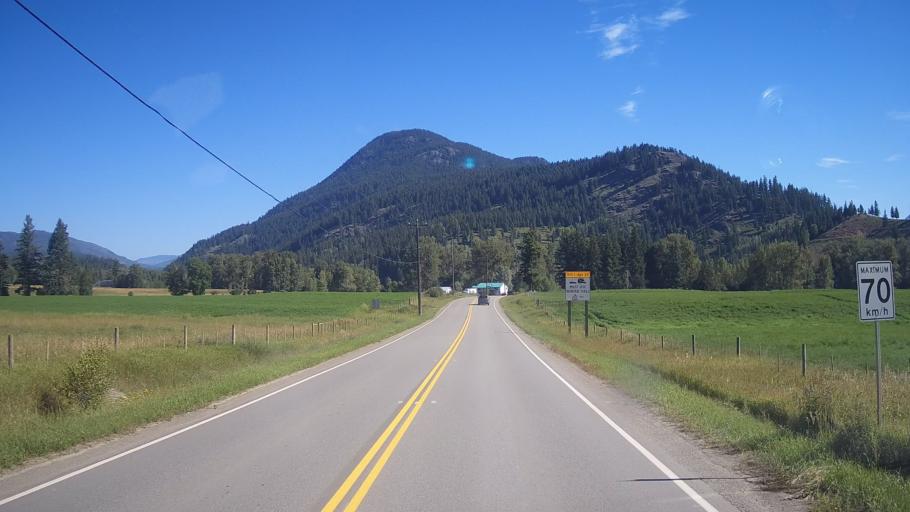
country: CA
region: British Columbia
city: Kamloops
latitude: 51.4282
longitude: -120.2110
